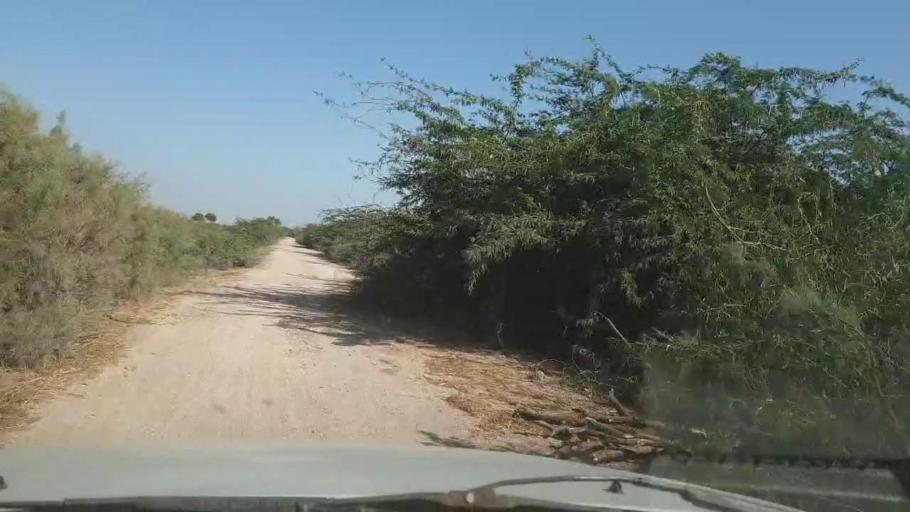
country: PK
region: Sindh
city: Mirpur Sakro
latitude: 24.4655
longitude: 67.7654
